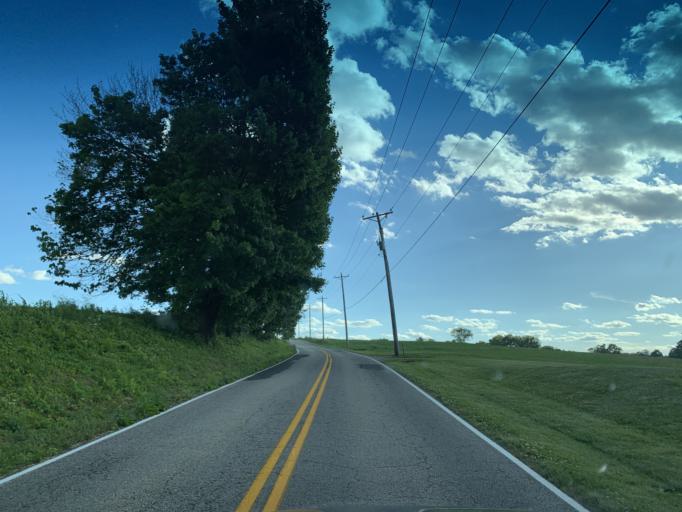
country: US
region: Maryland
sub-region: Cecil County
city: Rising Sun
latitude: 39.6367
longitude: -76.0466
